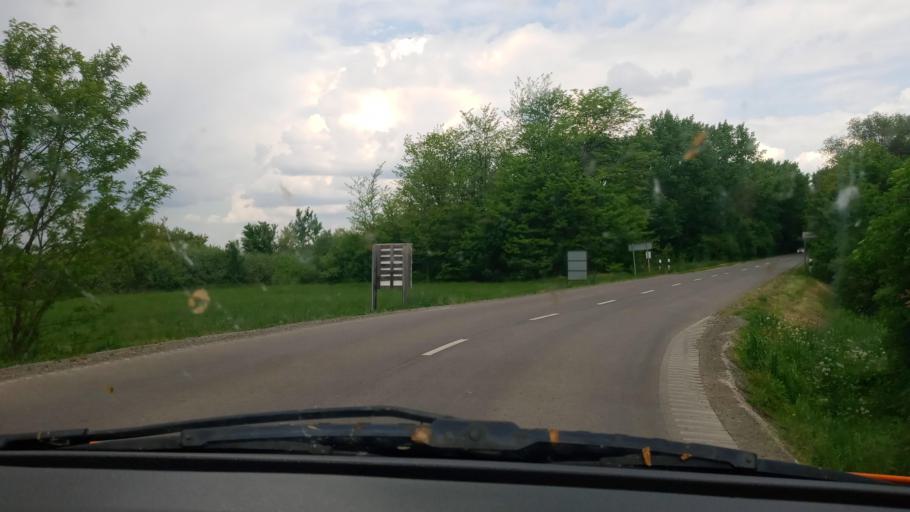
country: HU
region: Baranya
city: Villany
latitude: 45.8520
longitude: 18.4803
